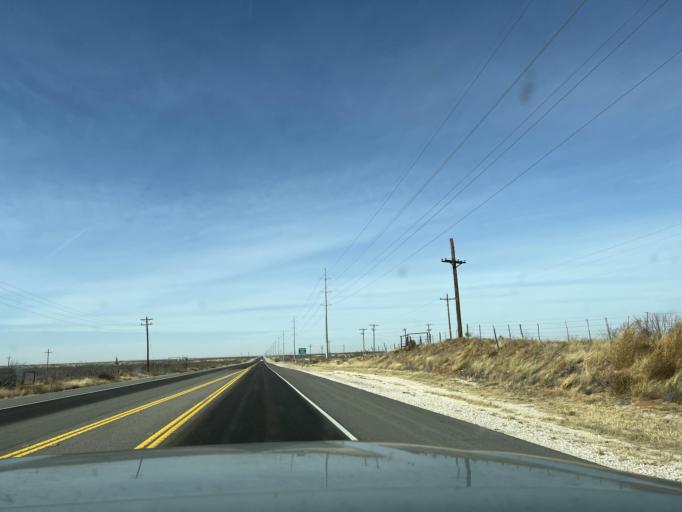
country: US
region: Texas
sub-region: Andrews County
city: Andrews
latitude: 32.3345
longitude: -102.6602
